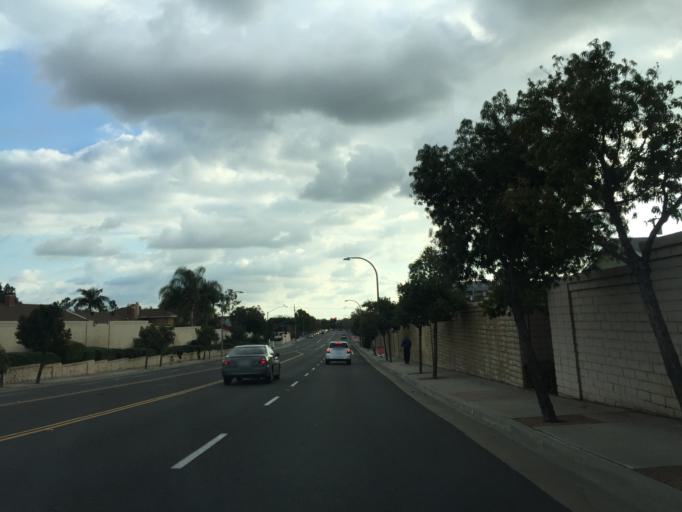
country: US
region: California
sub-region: Orange County
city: Brea
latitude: 33.9238
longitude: -117.8829
